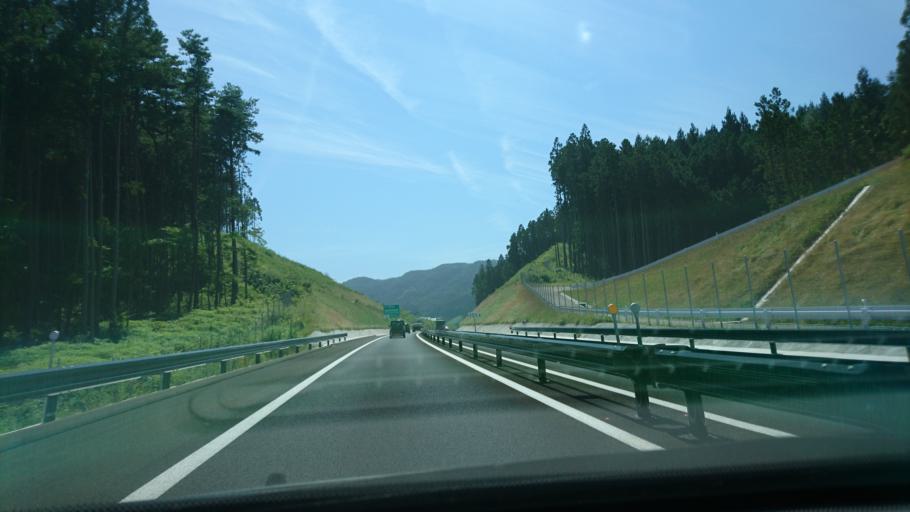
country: JP
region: Iwate
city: Ofunato
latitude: 38.9973
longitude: 141.6149
